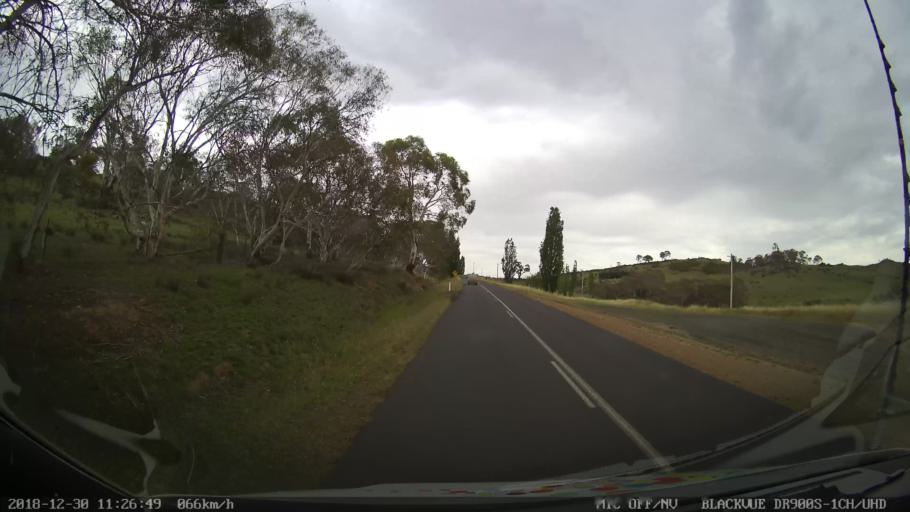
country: AU
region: New South Wales
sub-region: Snowy River
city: Jindabyne
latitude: -36.4653
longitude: 148.6308
